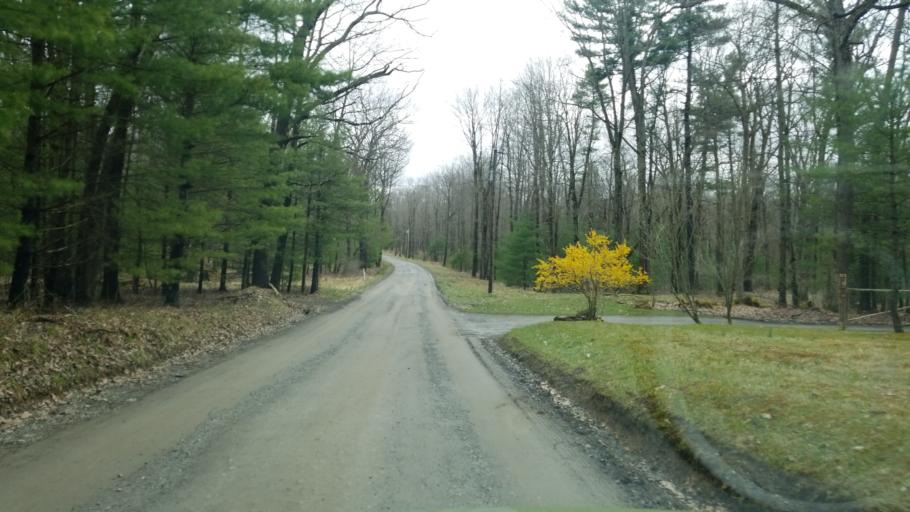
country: US
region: Pennsylvania
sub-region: Clearfield County
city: Shiloh
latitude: 41.1788
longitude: -78.3289
